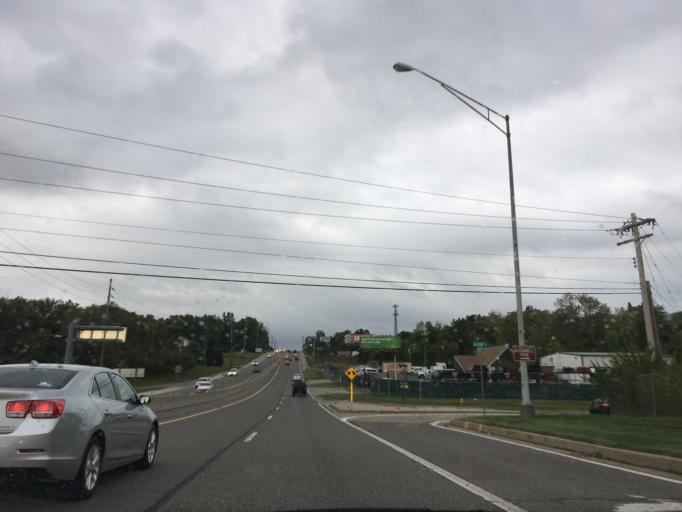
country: US
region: Missouri
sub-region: Saint Louis County
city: Maryland Heights
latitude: 38.7105
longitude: -90.4085
